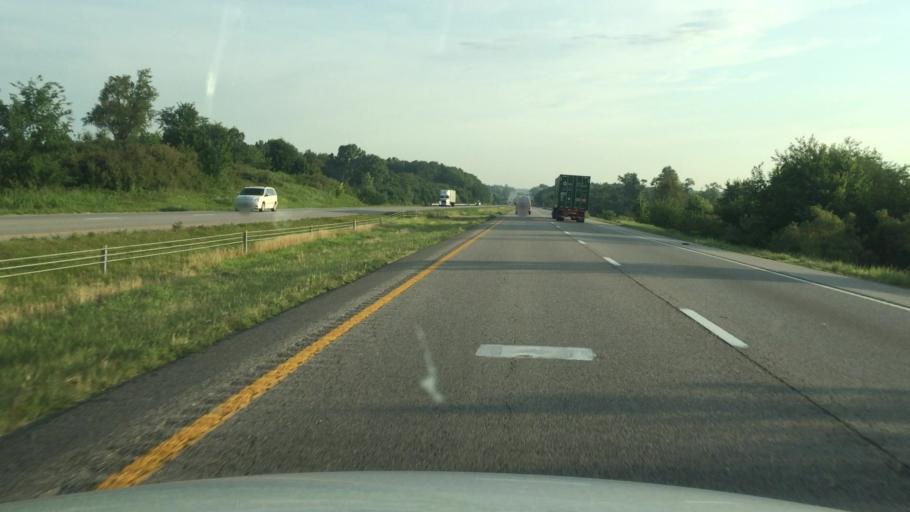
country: US
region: Missouri
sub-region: Platte County
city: Weston
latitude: 39.5596
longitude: -94.7880
